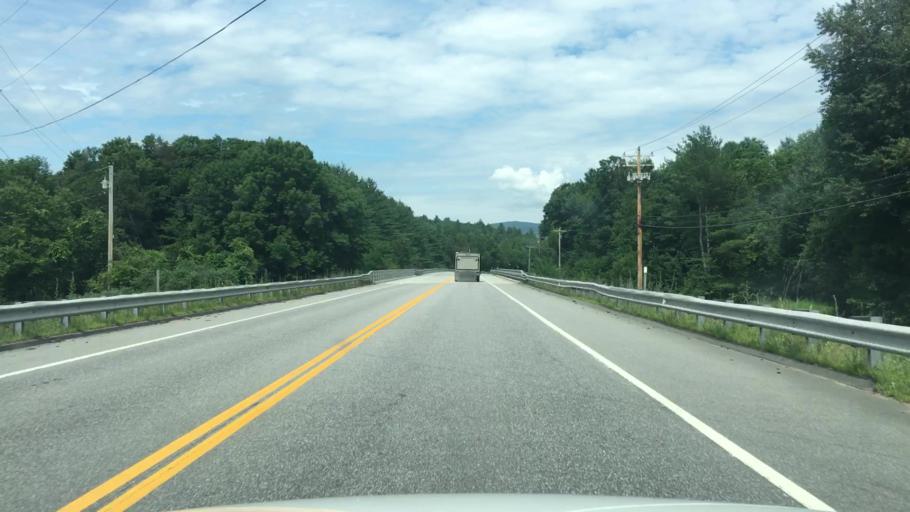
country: US
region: New Hampshire
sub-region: Grafton County
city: Rumney
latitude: 43.8455
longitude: -71.9102
